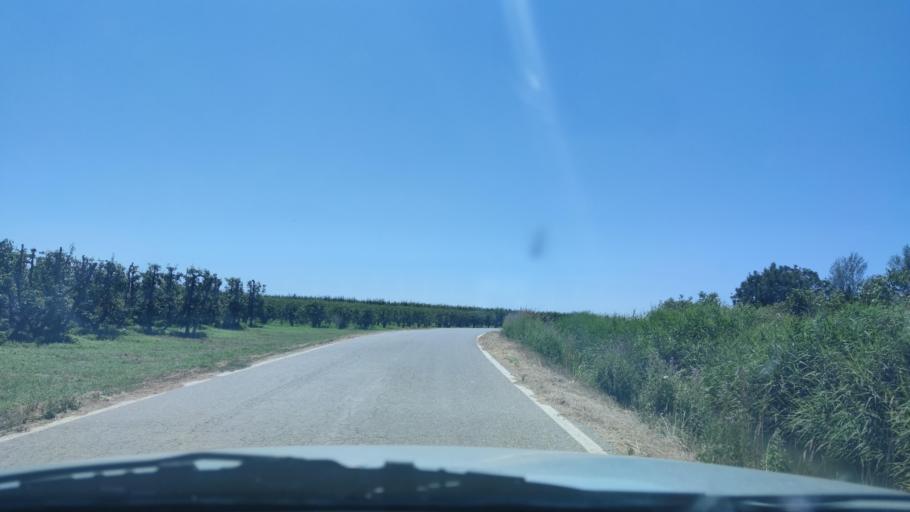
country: ES
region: Catalonia
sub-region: Provincia de Lleida
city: Alcoletge
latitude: 41.6555
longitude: 0.6797
